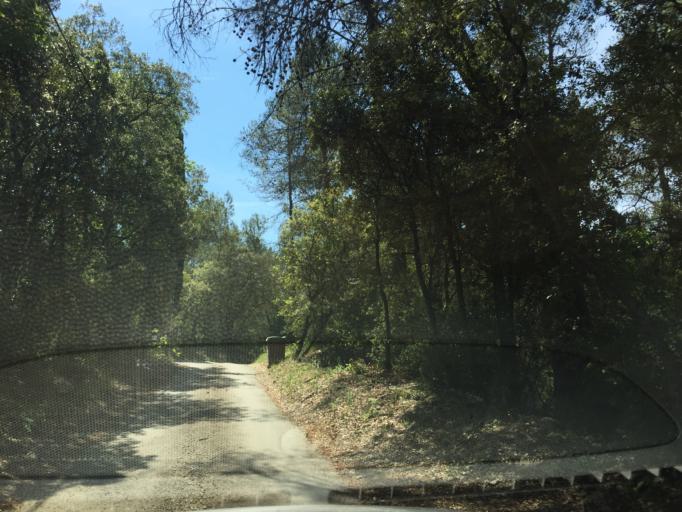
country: FR
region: Provence-Alpes-Cote d'Azur
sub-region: Departement du Var
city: Lorgues
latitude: 43.4746
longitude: 6.3690
